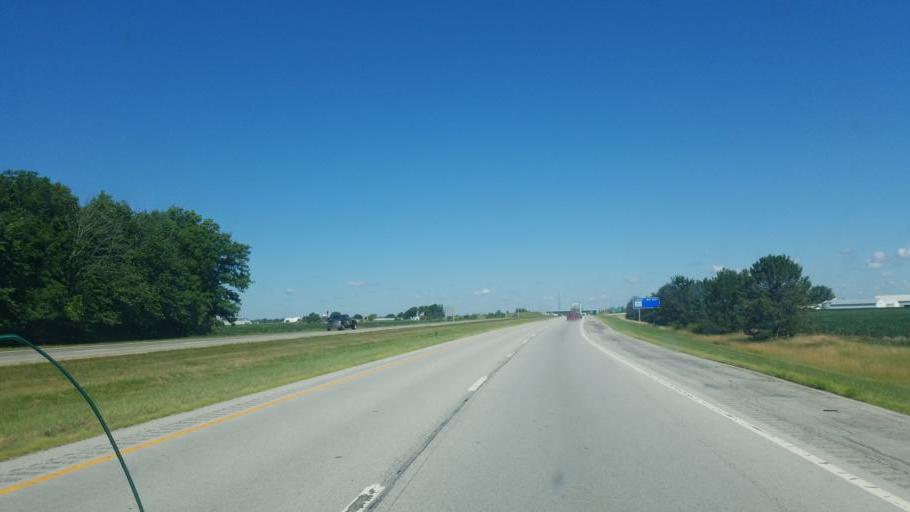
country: US
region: Ohio
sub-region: Allen County
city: Delphos
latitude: 40.8413
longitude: -84.3008
